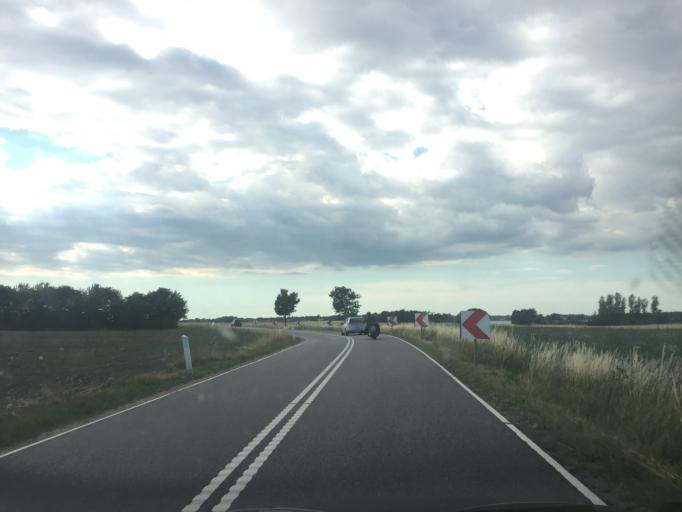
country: DK
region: Capital Region
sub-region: Egedal Kommune
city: Stenlose
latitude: 55.7335
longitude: 12.1908
